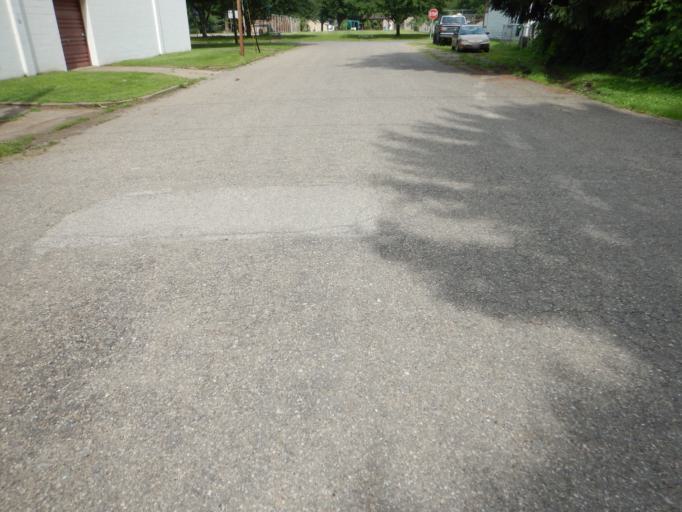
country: US
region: Ohio
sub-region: Muskingum County
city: South Zanesville
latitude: 39.9178
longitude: -82.0071
